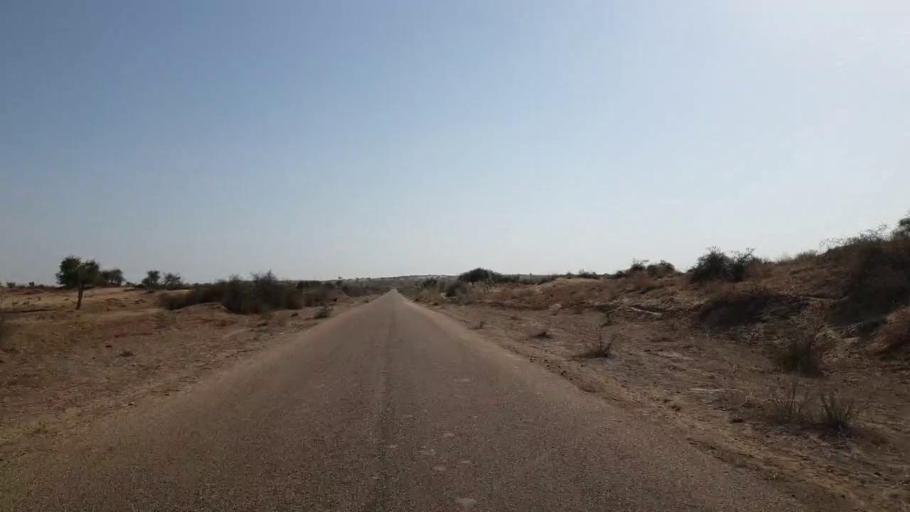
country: PK
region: Sindh
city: Islamkot
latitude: 25.0729
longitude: 70.0430
